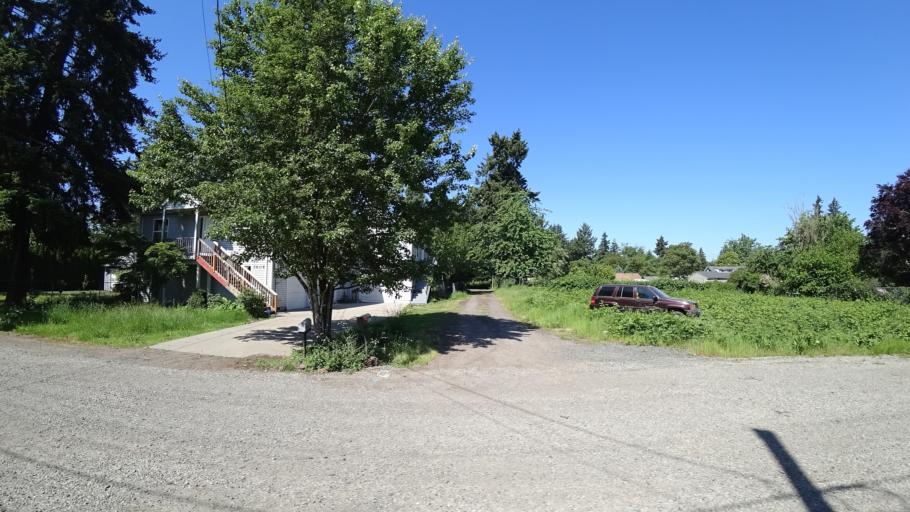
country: US
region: Oregon
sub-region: Multnomah County
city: Lents
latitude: 45.4822
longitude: -122.5430
